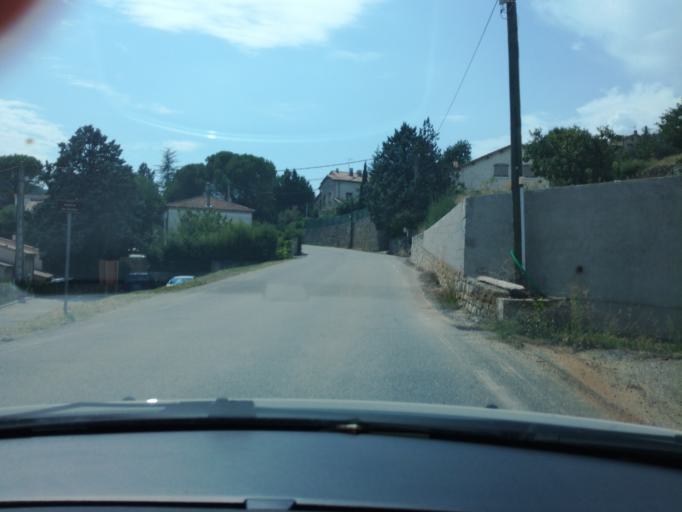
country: FR
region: Rhone-Alpes
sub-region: Departement de l'Ardeche
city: Labegude
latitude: 44.6375
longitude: 4.3687
